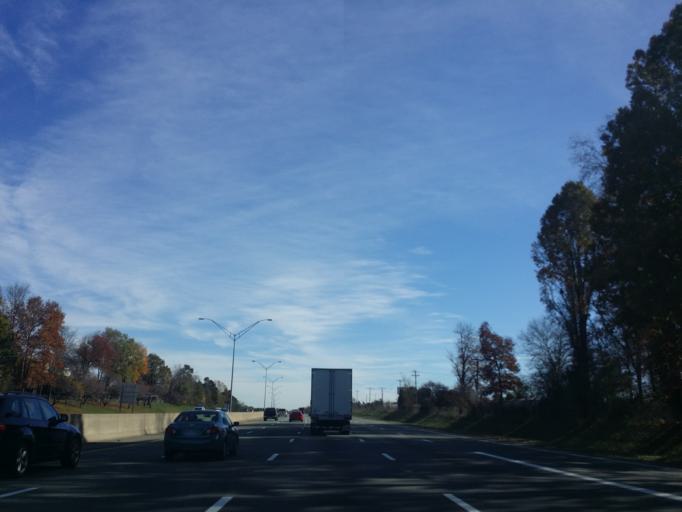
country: US
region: North Carolina
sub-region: Alamance County
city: Graham
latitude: 36.0632
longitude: -79.4267
